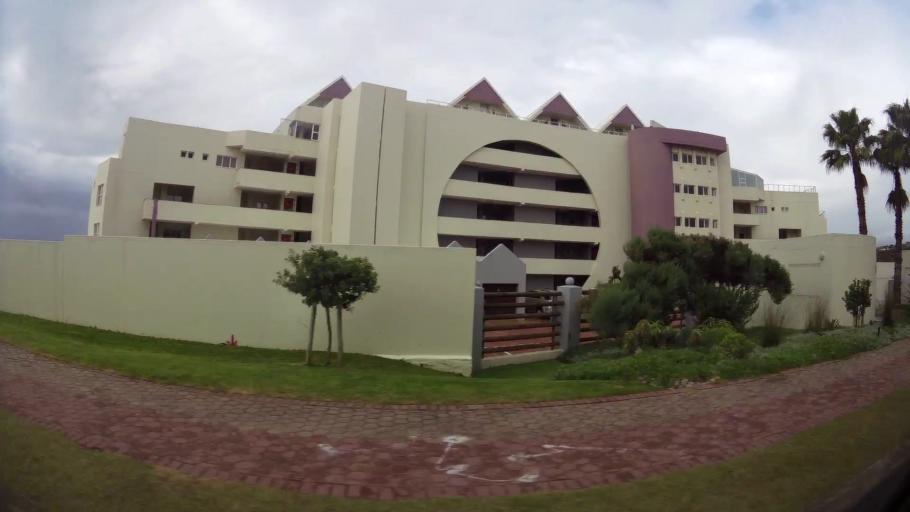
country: ZA
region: Western Cape
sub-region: Eden District Municipality
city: Mossel Bay
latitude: -34.1610
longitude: 22.1094
